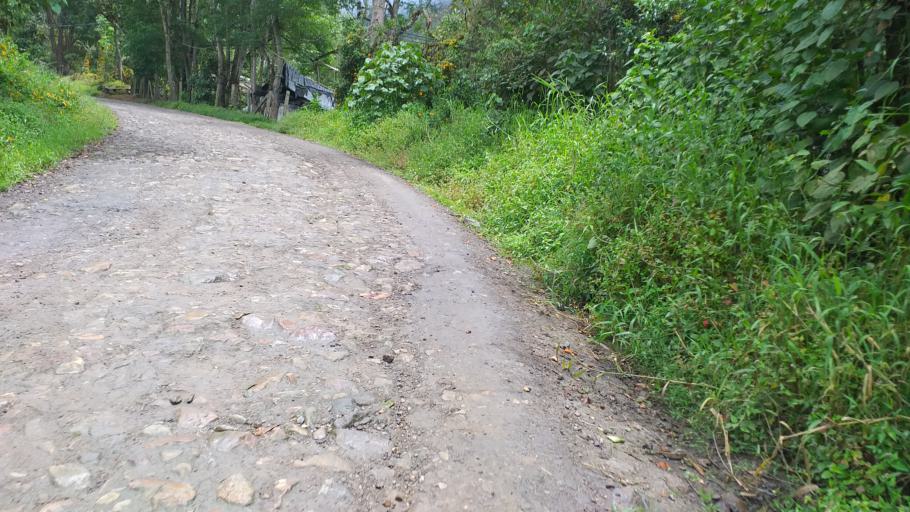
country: CO
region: Cundinamarca
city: Tenza
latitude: 5.1074
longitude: -73.4496
